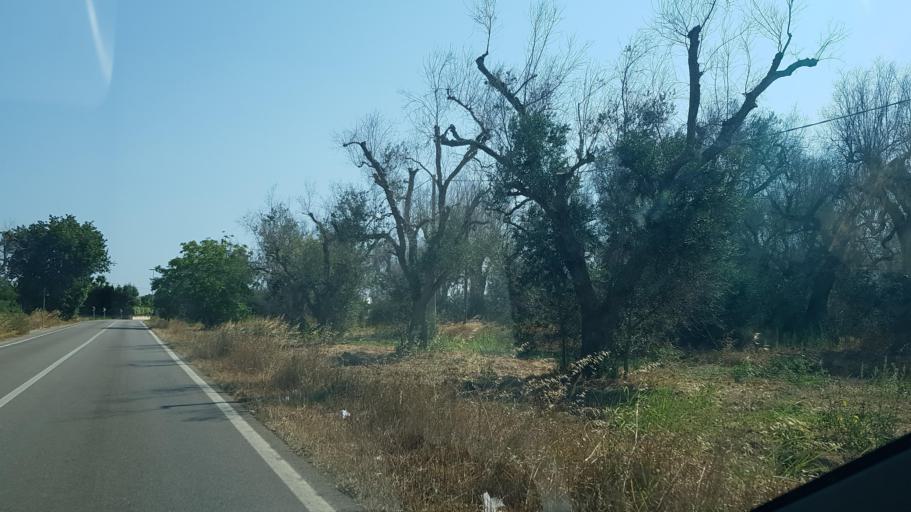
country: IT
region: Apulia
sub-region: Provincia di Lecce
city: Ruffano
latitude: 39.9957
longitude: 18.2639
